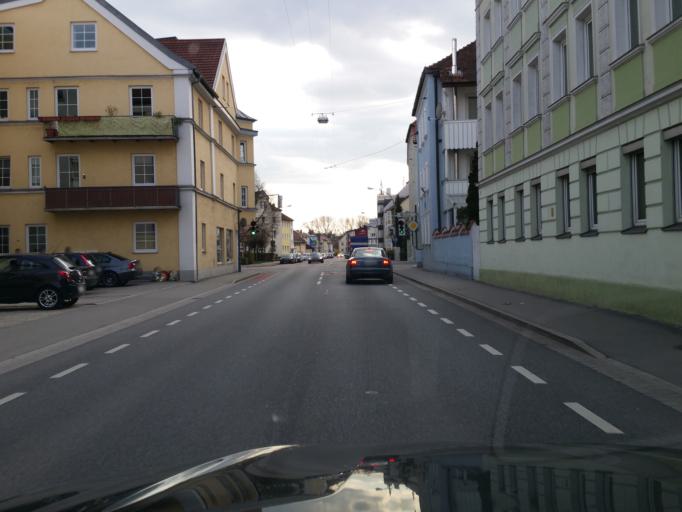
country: DE
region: Bavaria
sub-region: Lower Bavaria
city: Landshut
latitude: 48.5426
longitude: 12.1439
